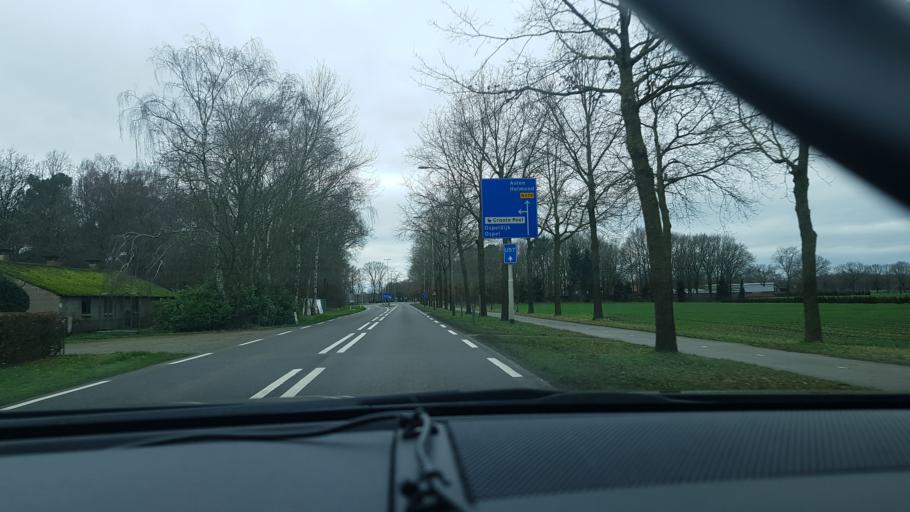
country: NL
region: Limburg
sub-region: Gemeente Leudal
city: Heythuysen
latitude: 51.3463
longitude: 5.8692
